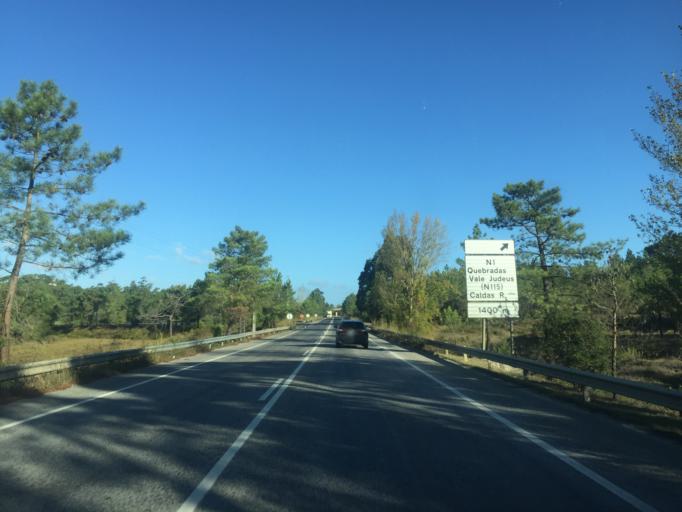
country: PT
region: Lisbon
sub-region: Azambuja
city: Alcoentre
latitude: 39.2205
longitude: -8.9544
